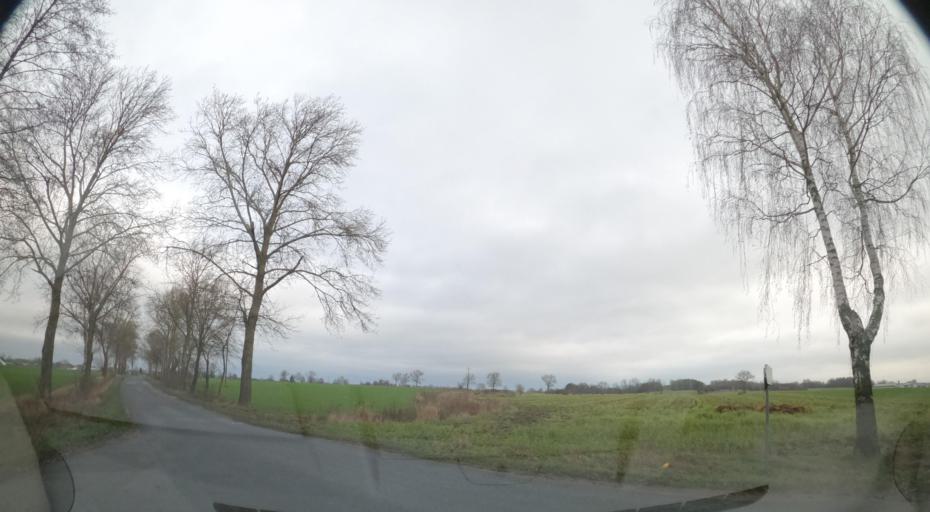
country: PL
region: Greater Poland Voivodeship
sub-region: Powiat pilski
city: Wysoka
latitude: 53.2521
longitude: 17.1498
